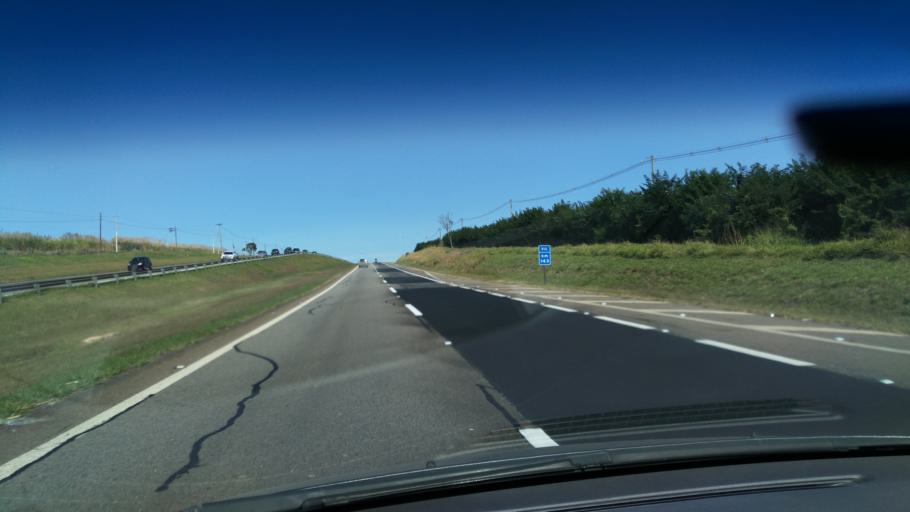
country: BR
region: Sao Paulo
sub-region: Santo Antonio De Posse
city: Santo Antonio de Posse
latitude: -22.5985
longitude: -47.0081
